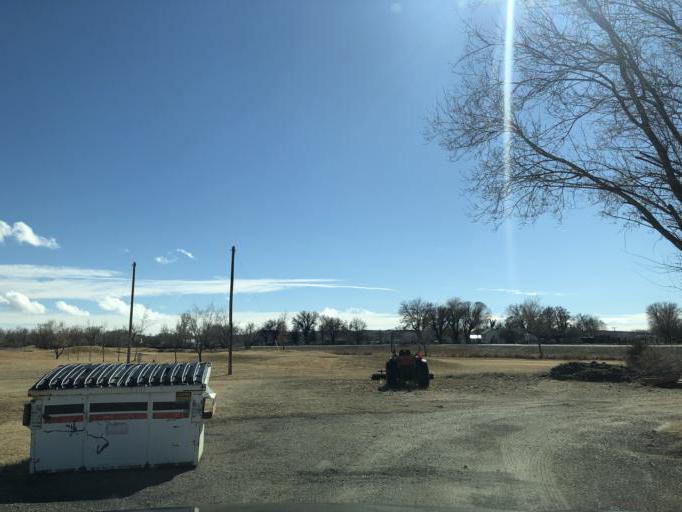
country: US
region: Utah
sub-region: Carbon County
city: East Carbon City
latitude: 38.9936
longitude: -110.1559
